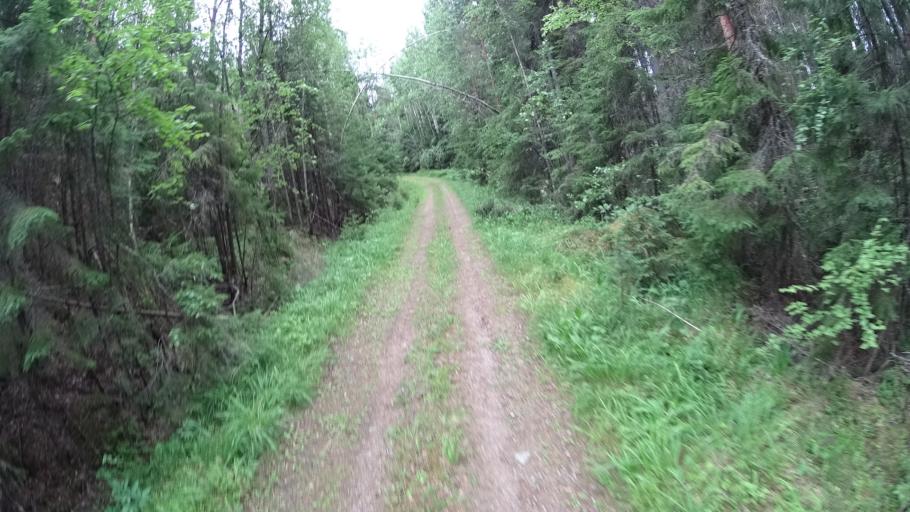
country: FI
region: Southern Savonia
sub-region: Mikkeli
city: Maentyharju
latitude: 61.1743
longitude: 26.8970
